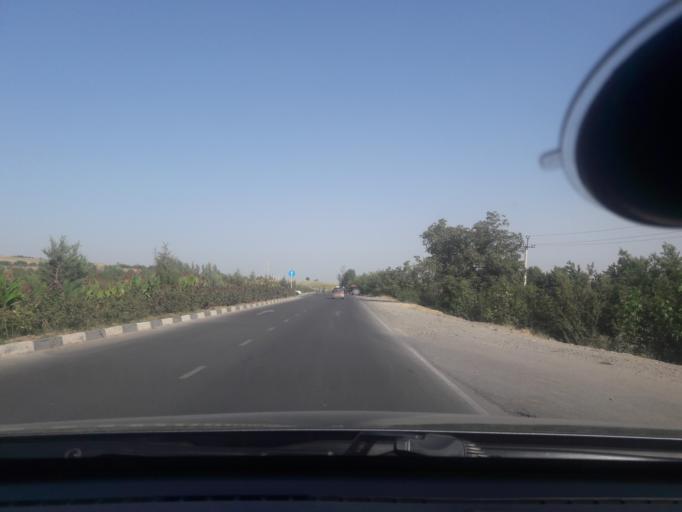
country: TJ
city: Shahrinav
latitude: 38.5740
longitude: 68.3621
